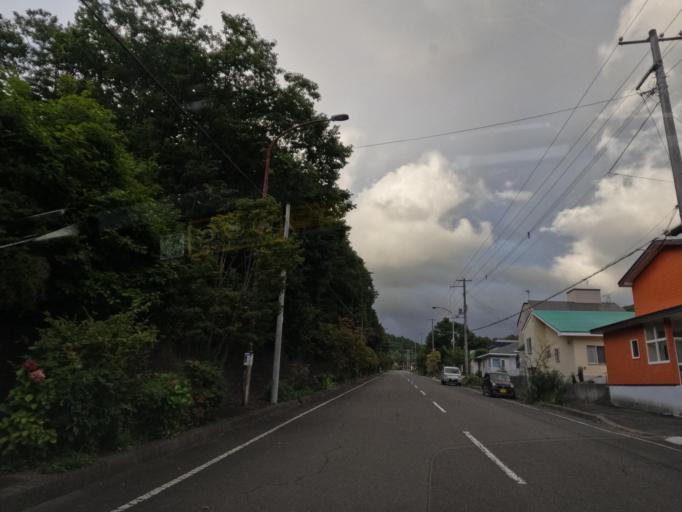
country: JP
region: Hokkaido
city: Muroran
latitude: 42.3721
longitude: 140.9559
